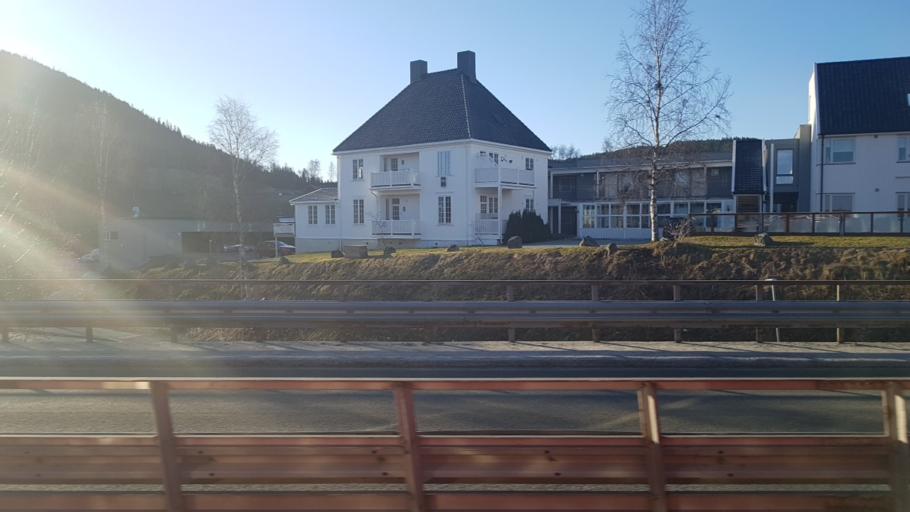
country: NO
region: Sor-Trondelag
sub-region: Malvik
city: Hommelvik
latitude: 63.4149
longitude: 10.7900
